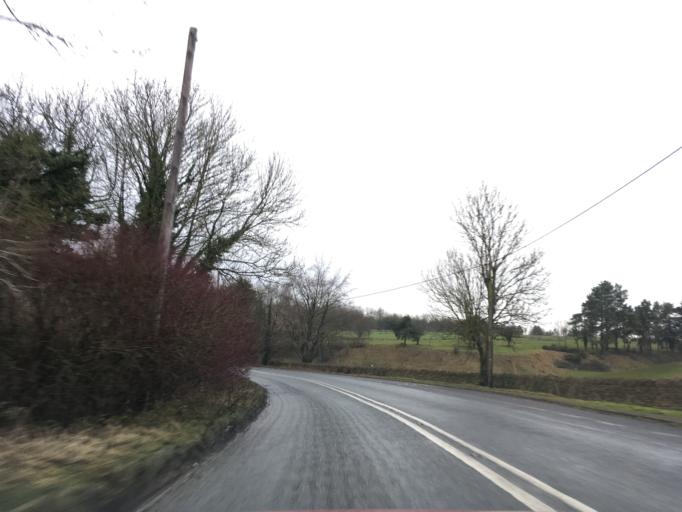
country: GB
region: England
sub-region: Gloucestershire
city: Cirencester
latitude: 51.7429
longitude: -1.9738
